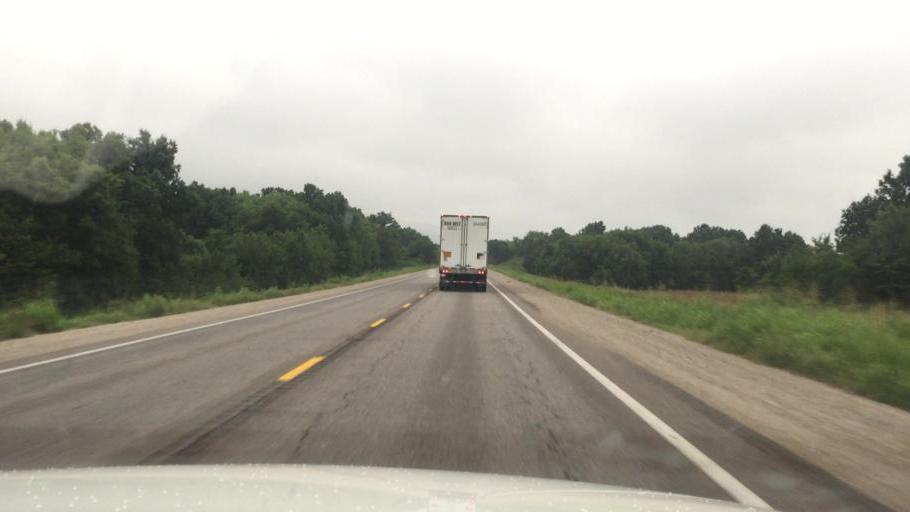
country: US
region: Kansas
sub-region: Montgomery County
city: Cherryvale
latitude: 37.1646
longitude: -95.5767
